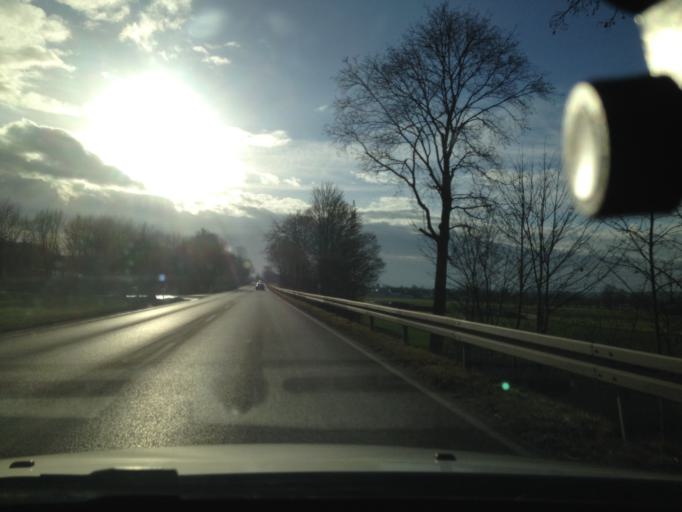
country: DE
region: Bavaria
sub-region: Swabia
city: Wehringen
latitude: 48.2566
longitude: 10.8120
